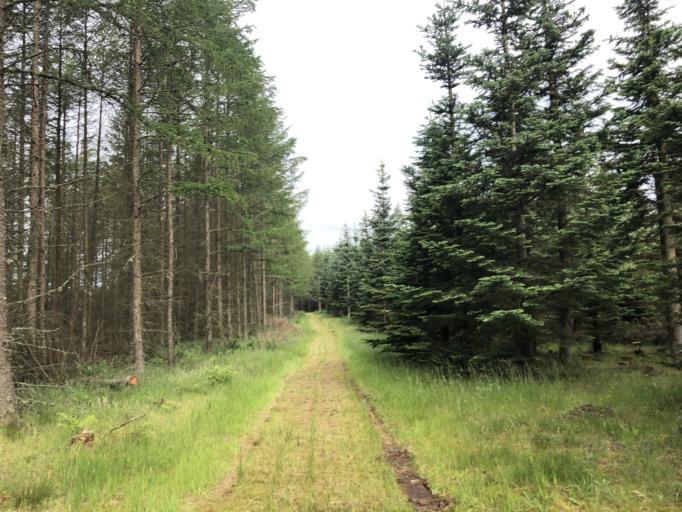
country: DK
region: Central Jutland
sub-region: Holstebro Kommune
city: Ulfborg
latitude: 56.2378
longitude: 8.3996
